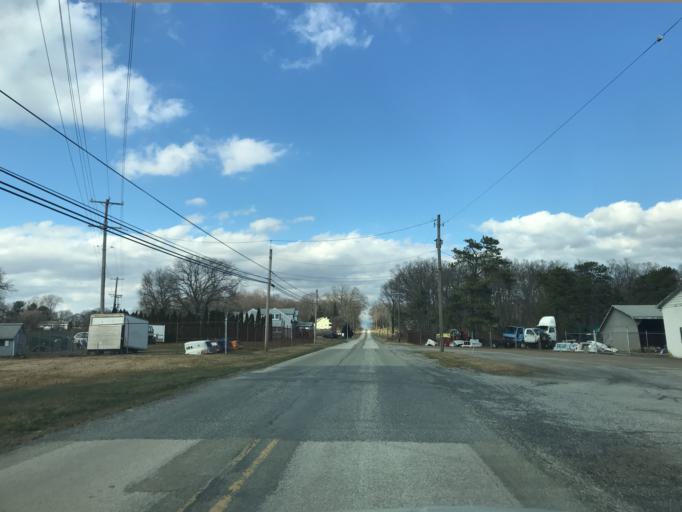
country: US
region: Maryland
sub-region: Cecil County
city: Rising Sun
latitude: 39.7388
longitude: -76.0227
